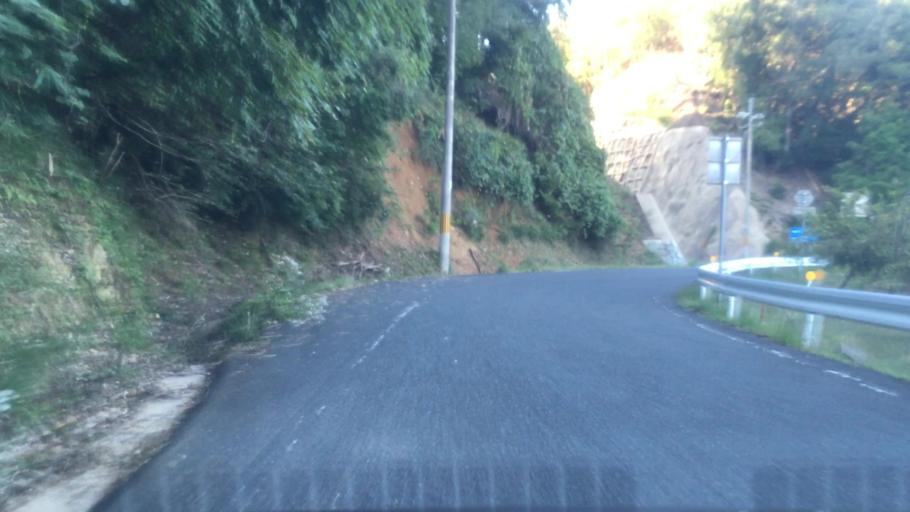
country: JP
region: Hyogo
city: Toyooka
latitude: 35.6183
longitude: 134.8731
